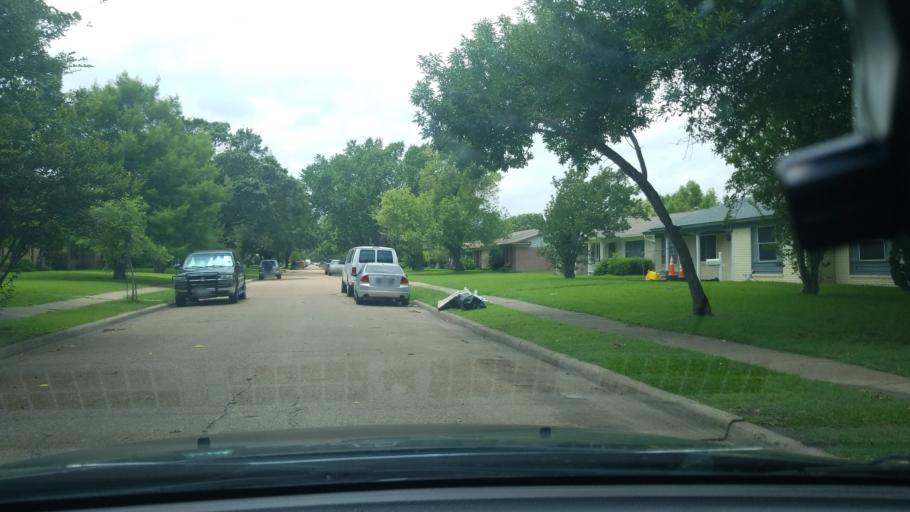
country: US
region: Texas
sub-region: Dallas County
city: Mesquite
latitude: 32.7949
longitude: -96.6458
